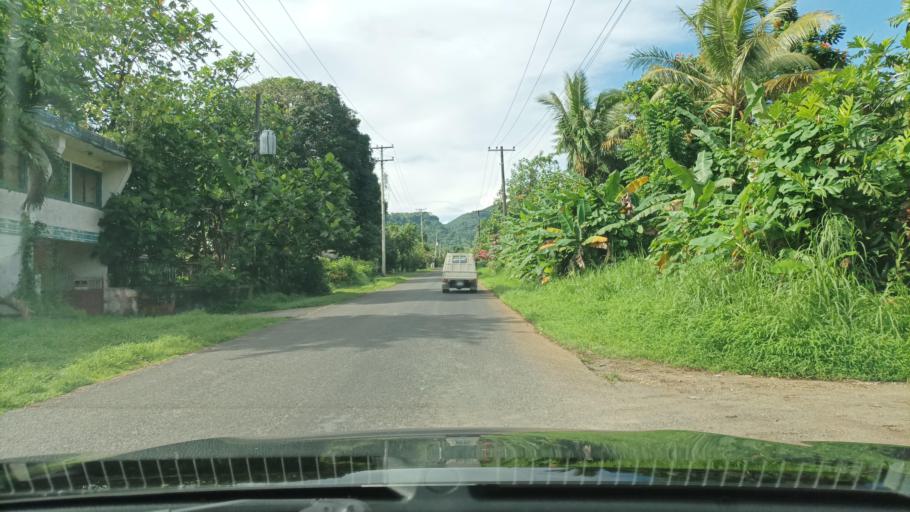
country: FM
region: Pohnpei
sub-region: Kolonia Municipality
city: Kolonia Town
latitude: 6.9467
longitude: 158.1951
